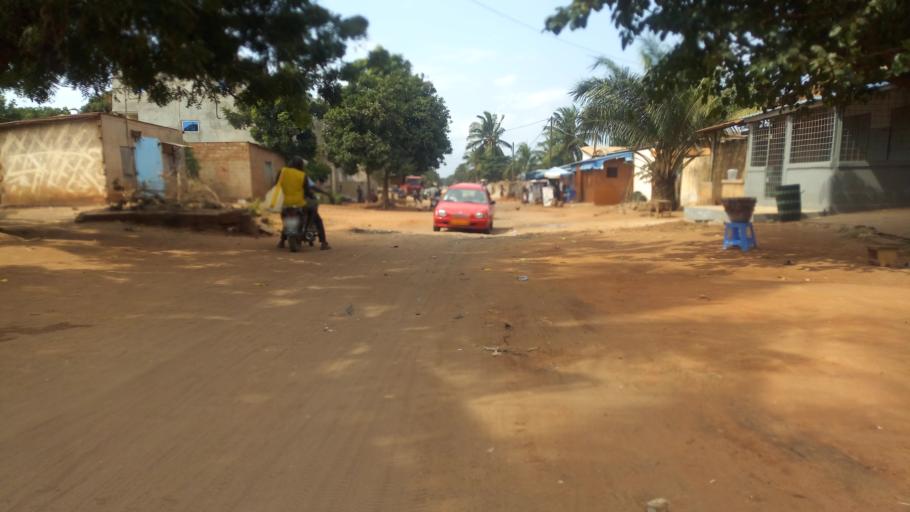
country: TG
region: Maritime
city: Lome
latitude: 6.2271
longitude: 1.1803
